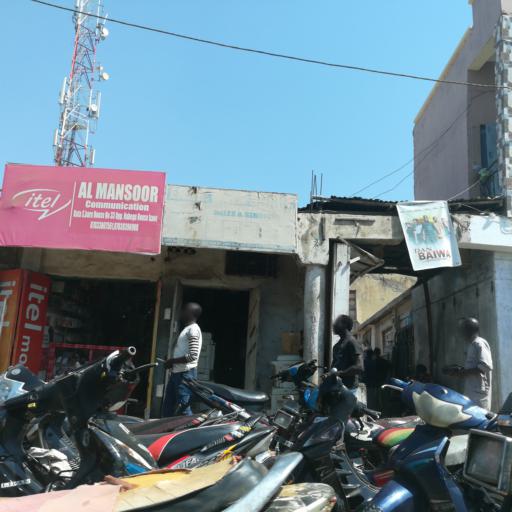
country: NG
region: Kano
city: Kano
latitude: 12.0090
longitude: 8.5392
